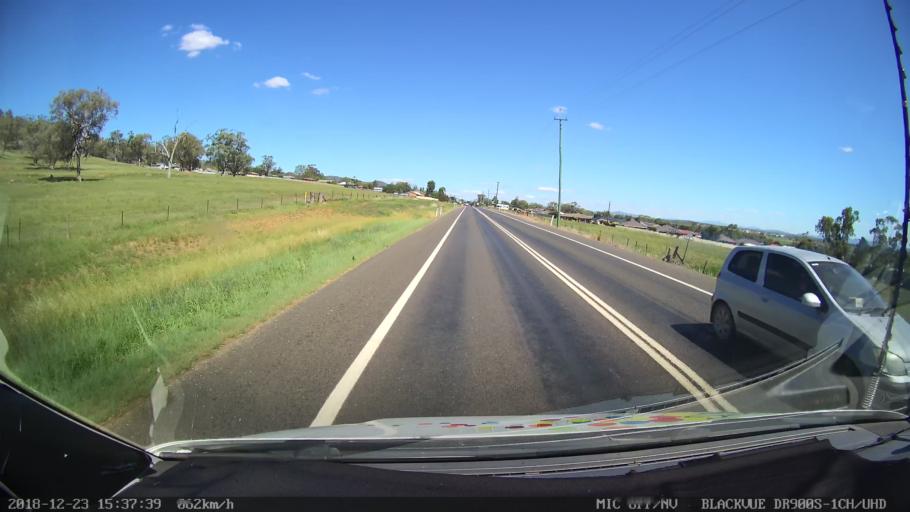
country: AU
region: New South Wales
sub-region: Tamworth Municipality
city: Tamworth
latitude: -31.0539
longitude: 150.8912
